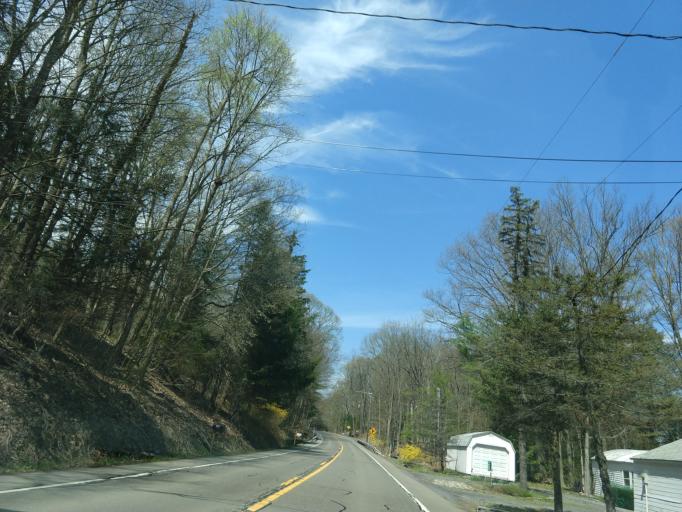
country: US
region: New York
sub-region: Tompkins County
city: Trumansburg
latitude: 42.5388
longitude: -76.5900
